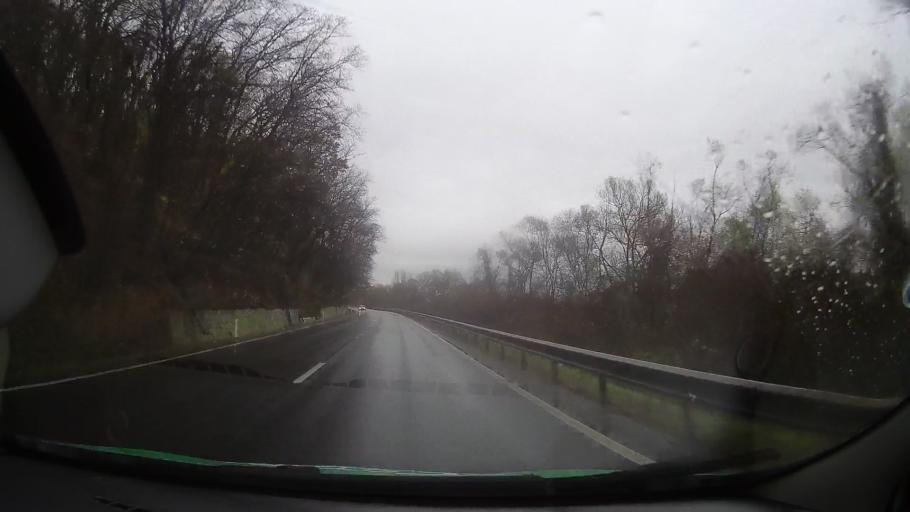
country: RO
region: Mures
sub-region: Comuna Brancovenesti
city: Brancovenesti
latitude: 46.8696
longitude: 24.7710
